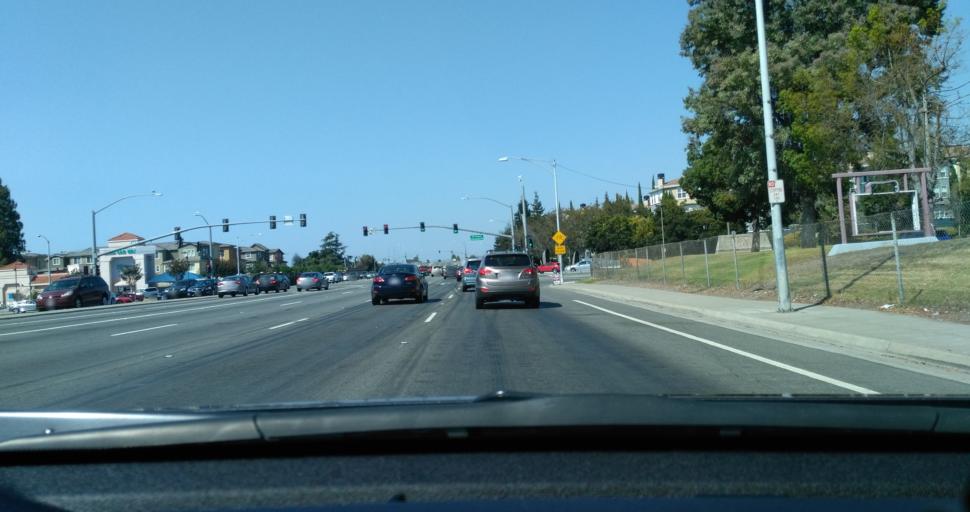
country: US
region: California
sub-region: Santa Clara County
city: Sunnyvale
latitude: 37.3860
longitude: -121.9957
